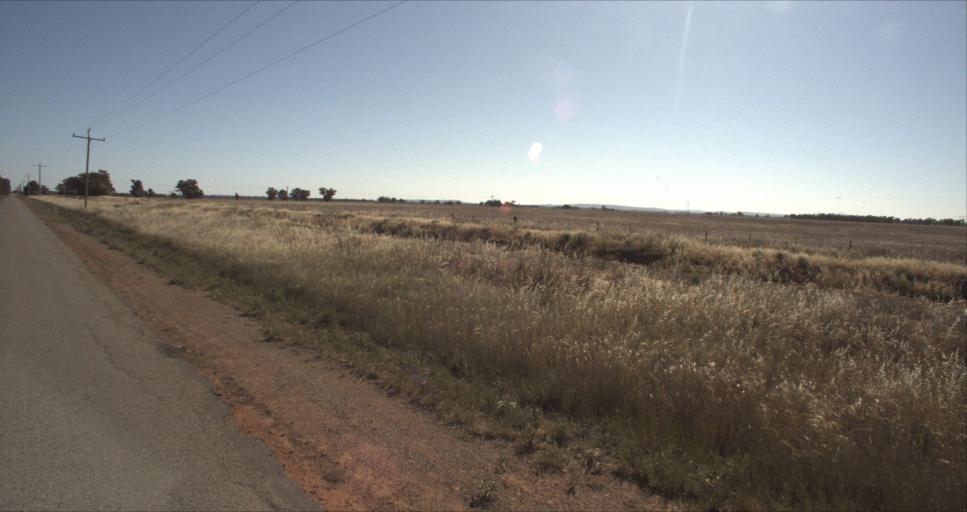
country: AU
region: New South Wales
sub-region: Leeton
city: Leeton
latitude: -34.5807
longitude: 146.3088
